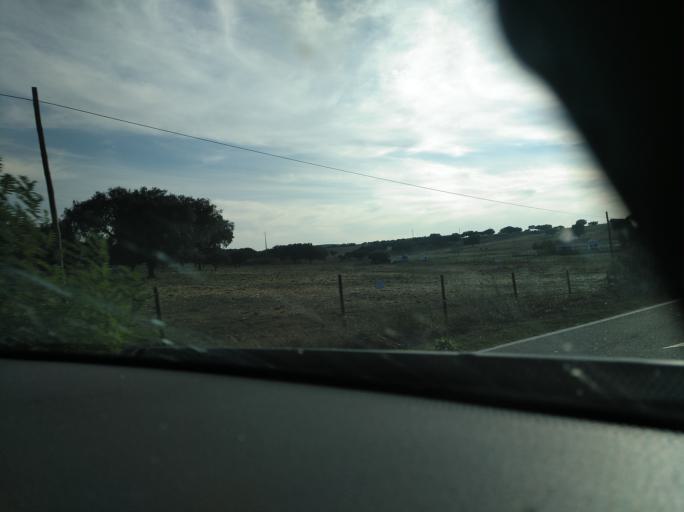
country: PT
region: Portalegre
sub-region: Fronteira
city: Fronteira
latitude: 38.9577
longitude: -7.6457
